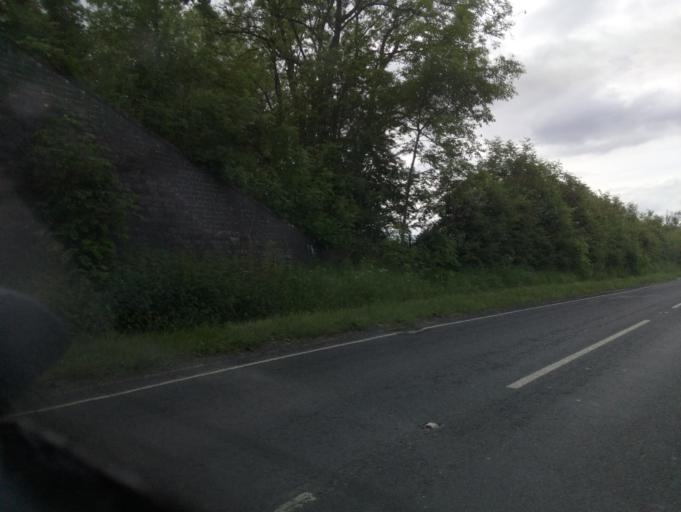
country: GB
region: England
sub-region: Worcestershire
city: Kempsey
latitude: 52.1561
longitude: -2.1547
